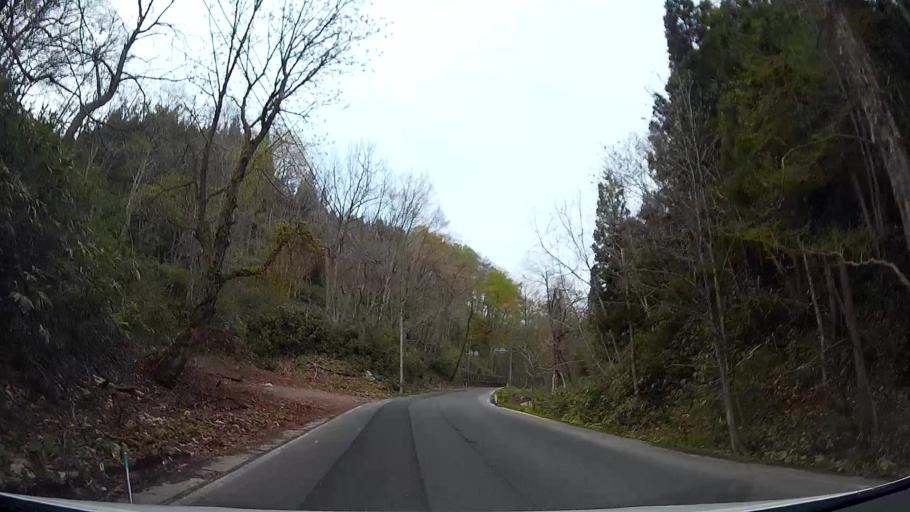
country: JP
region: Akita
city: Hanawa
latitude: 40.3816
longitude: 140.8885
